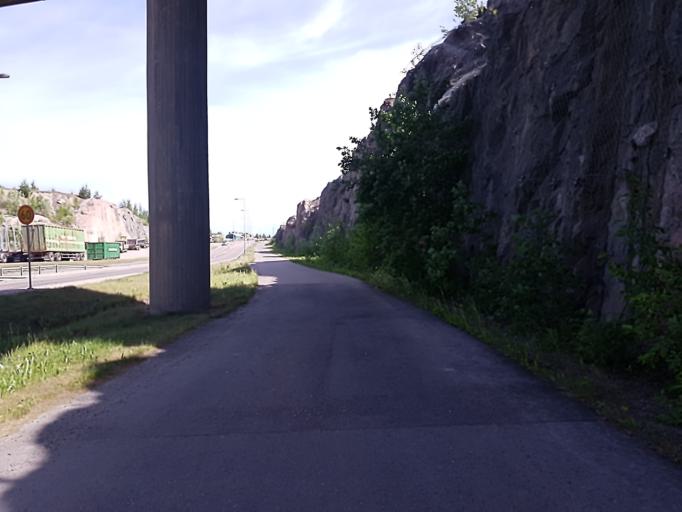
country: FI
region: Uusimaa
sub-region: Helsinki
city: Teekkarikylae
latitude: 60.3081
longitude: 24.8930
